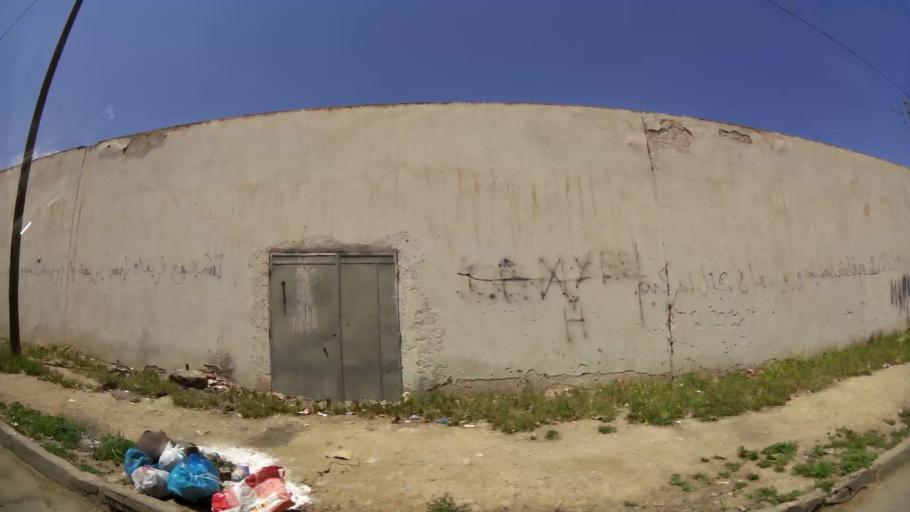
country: MA
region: Oriental
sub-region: Oujda-Angad
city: Oujda
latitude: 34.6971
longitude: -1.8999
